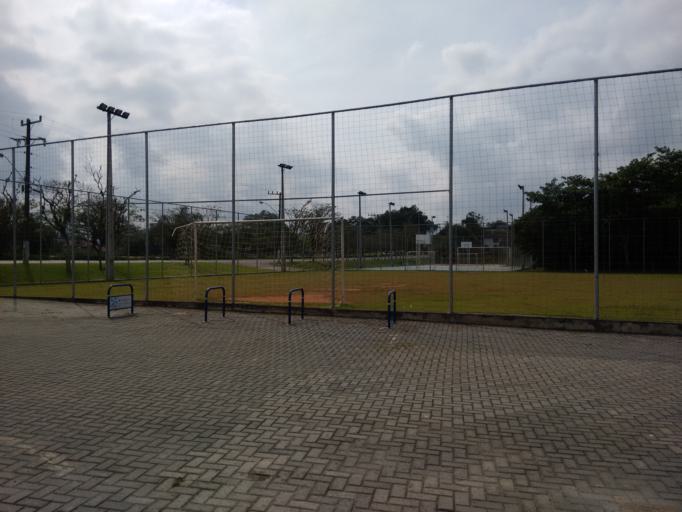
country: BR
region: Santa Catarina
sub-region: Timbo
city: Timbo
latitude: -26.8254
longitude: -49.2821
